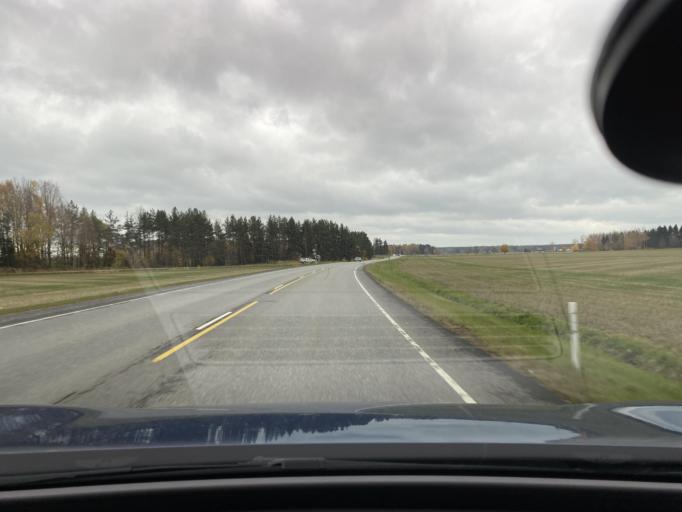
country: FI
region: Satakunta
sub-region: Rauma
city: Kiukainen
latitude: 61.1911
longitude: 22.0600
